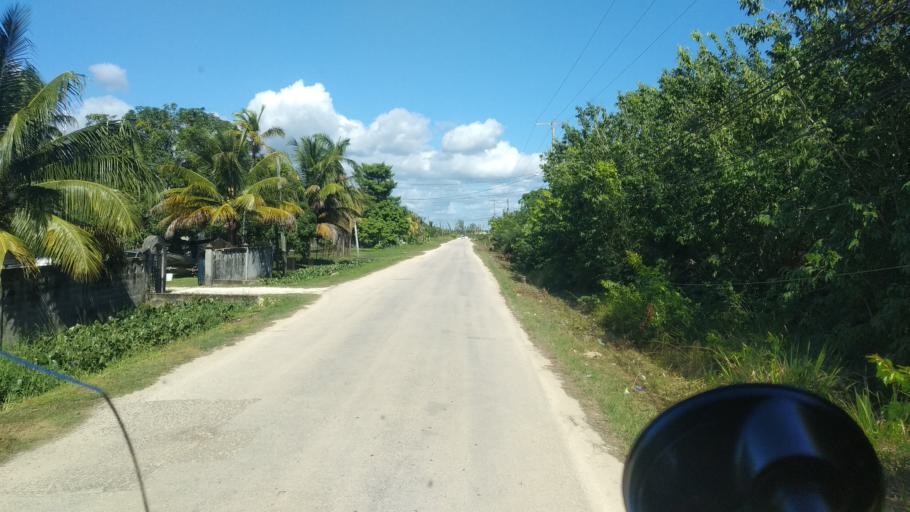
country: BZ
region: Belize
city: Belize City
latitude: 17.5575
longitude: -88.3025
